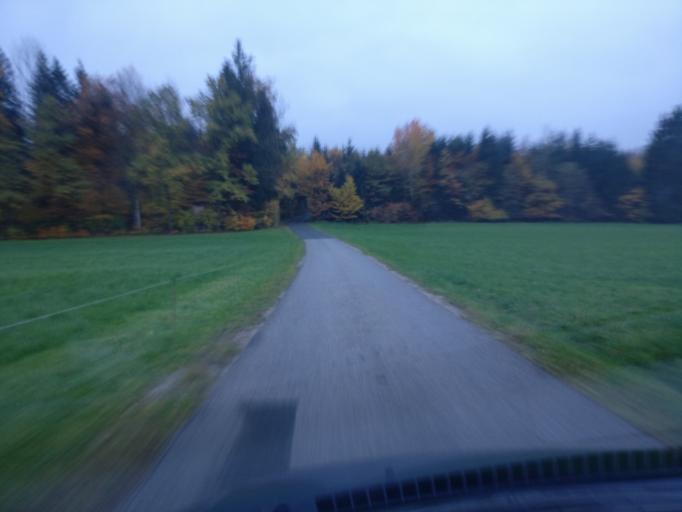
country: AT
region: Salzburg
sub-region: Politischer Bezirk Salzburg-Umgebung
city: Elixhausen
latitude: 47.8601
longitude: 13.0719
